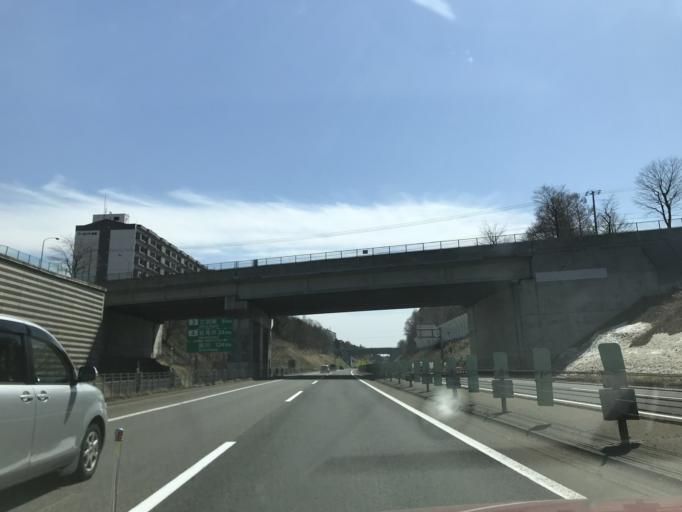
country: JP
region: Hokkaido
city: Ebetsu
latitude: 43.0910
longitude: 141.5062
